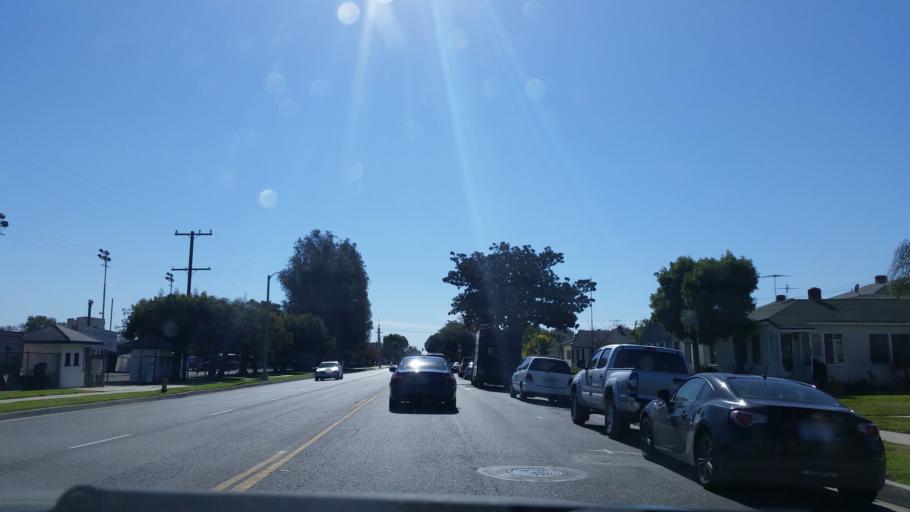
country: US
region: California
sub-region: Los Angeles County
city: Lakewood
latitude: 33.8459
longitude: -118.1338
